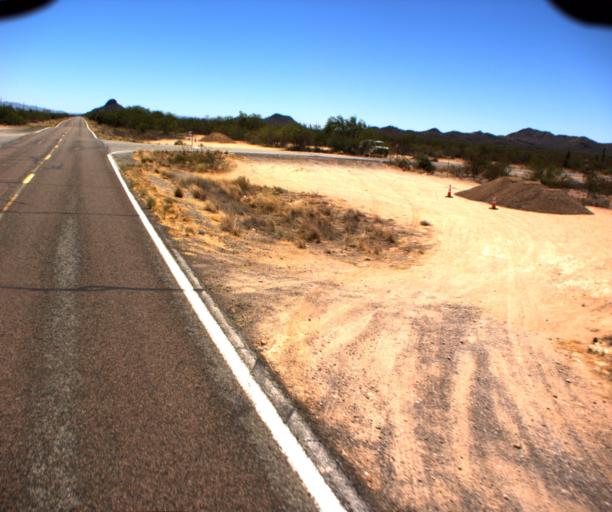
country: US
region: Arizona
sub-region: Pima County
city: Ajo
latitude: 32.2063
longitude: -112.5726
